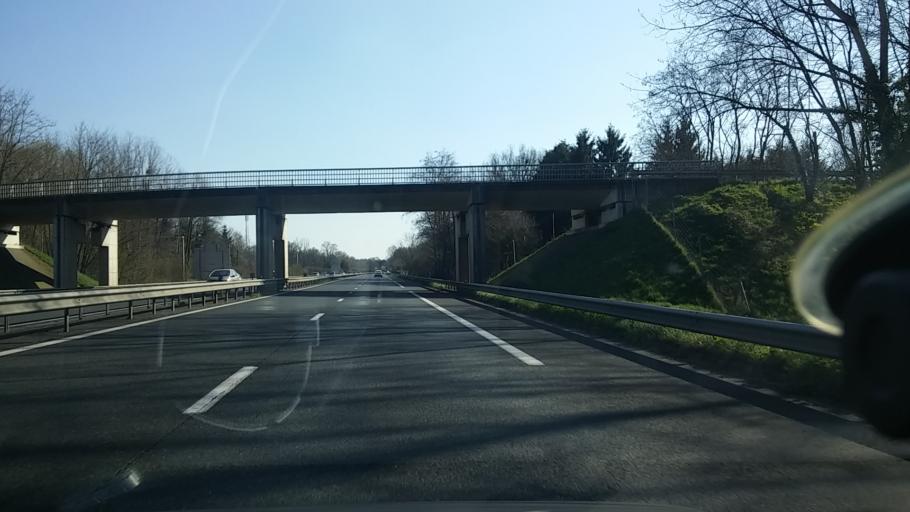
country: FR
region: Centre
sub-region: Departement du Cher
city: Vierzon
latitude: 47.2167
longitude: 2.0401
